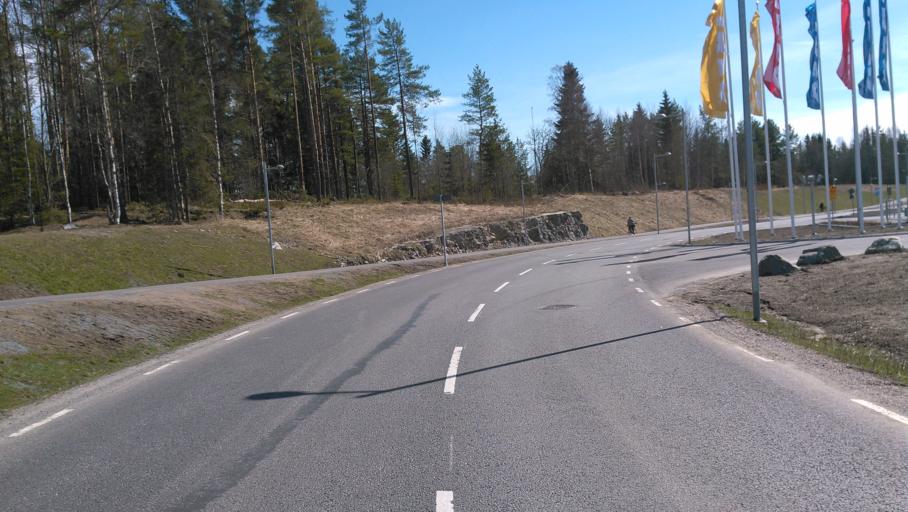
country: SE
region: Vaesterbotten
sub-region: Umea Kommun
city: Umea
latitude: 63.8090
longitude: 20.2575
